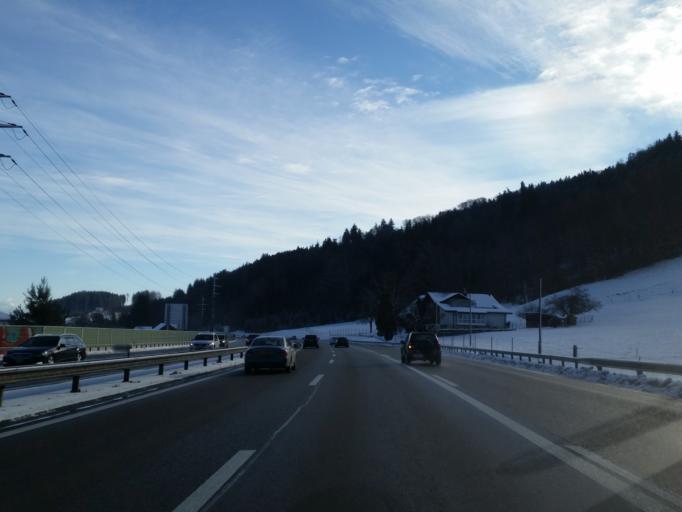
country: CH
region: Schwyz
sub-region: Bezirk Hoefe
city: Freienbach
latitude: 47.1947
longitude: 8.7624
